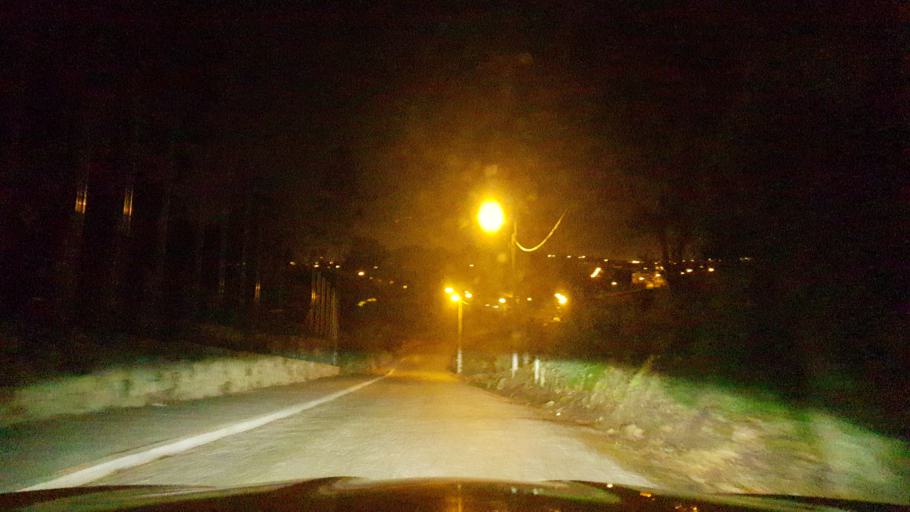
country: PT
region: Porto
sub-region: Matosinhos
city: Guifoes
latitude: 41.2185
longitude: -8.6620
